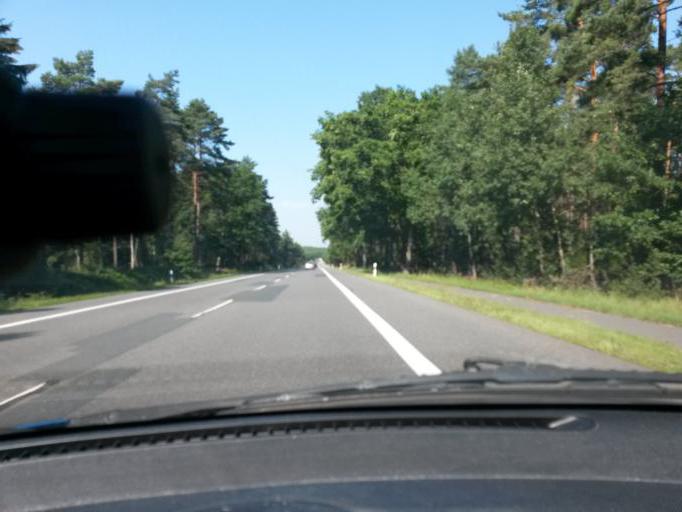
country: DE
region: Lower Saxony
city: Barendorf
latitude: 53.2326
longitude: 10.5005
